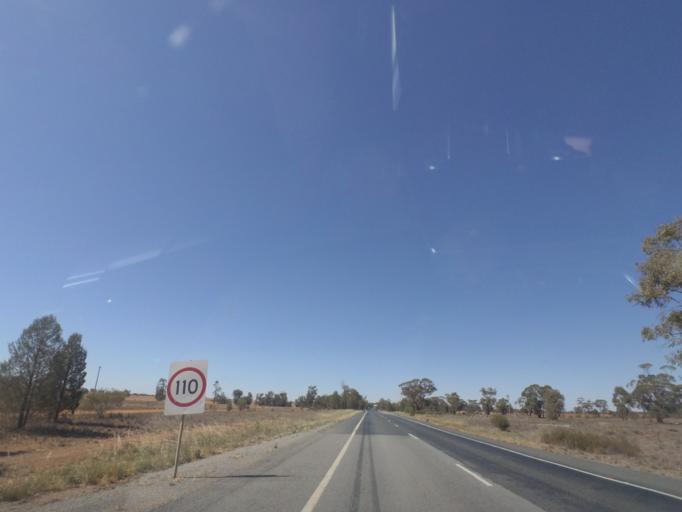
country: AU
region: New South Wales
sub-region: Bland
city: West Wyalong
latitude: -34.1960
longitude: 147.1109
